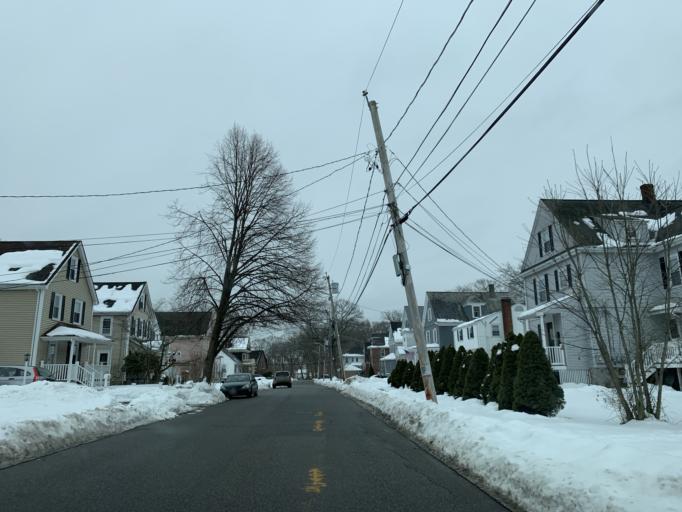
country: US
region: Massachusetts
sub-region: Norfolk County
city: Norwood
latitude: 42.1953
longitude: -71.2114
